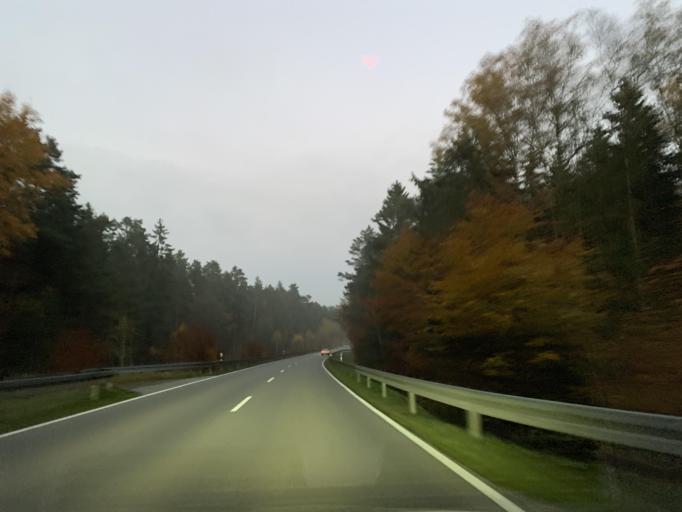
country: DE
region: Bavaria
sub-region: Upper Palatinate
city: Brunn
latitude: 49.2291
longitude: 12.1615
